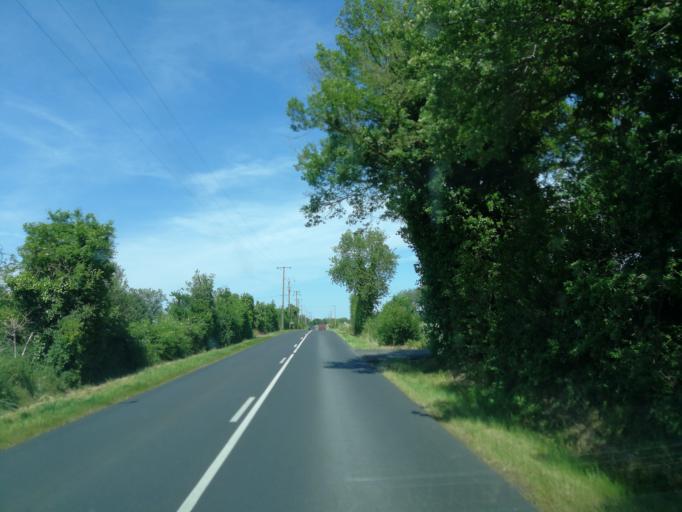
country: FR
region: Poitou-Charentes
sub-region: Departement des Deux-Sevres
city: Saint-Jean-de-Thouars
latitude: 46.9499
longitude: -0.2270
